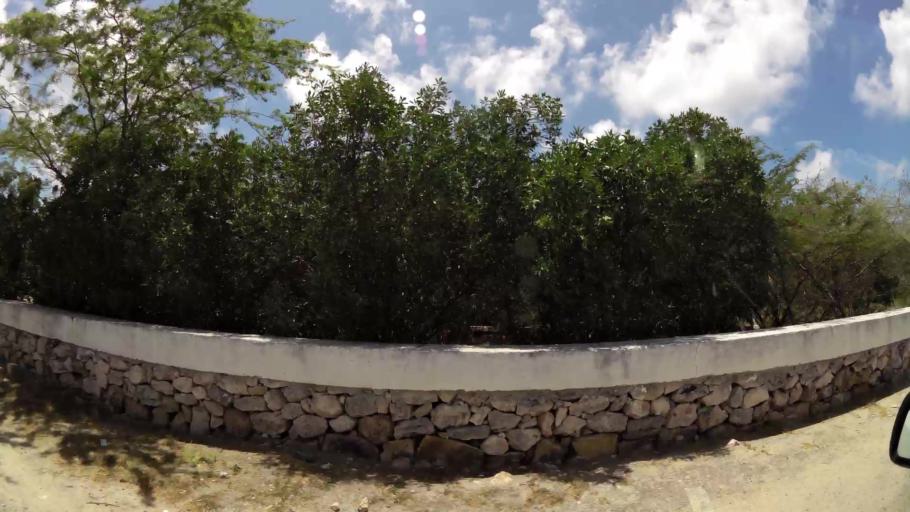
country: TC
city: Cockburn Town
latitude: 21.4625
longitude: -71.1420
